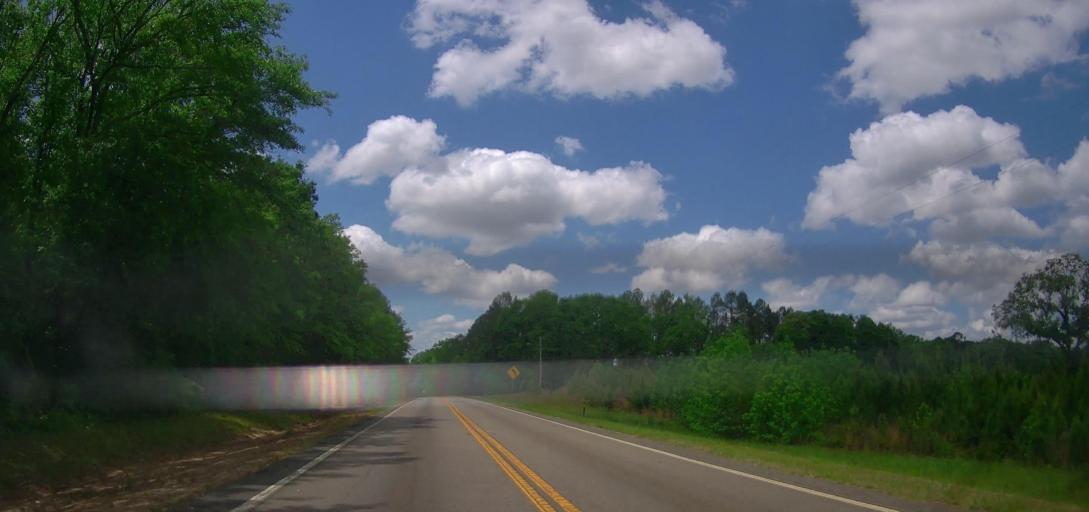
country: US
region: Georgia
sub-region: Dodge County
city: Chester
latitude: 32.5387
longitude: -83.1934
